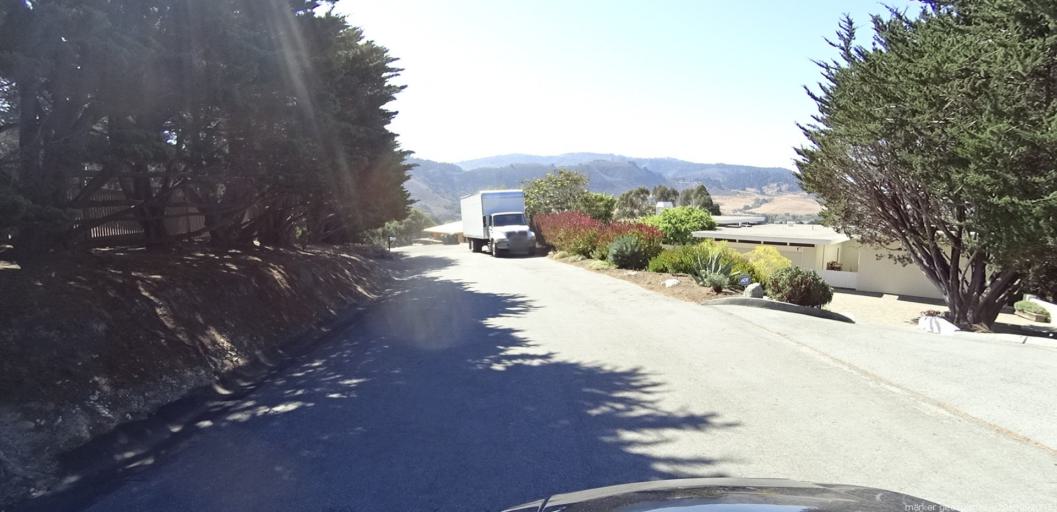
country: US
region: California
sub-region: Monterey County
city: Carmel-by-the-Sea
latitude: 36.5479
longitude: -121.9029
